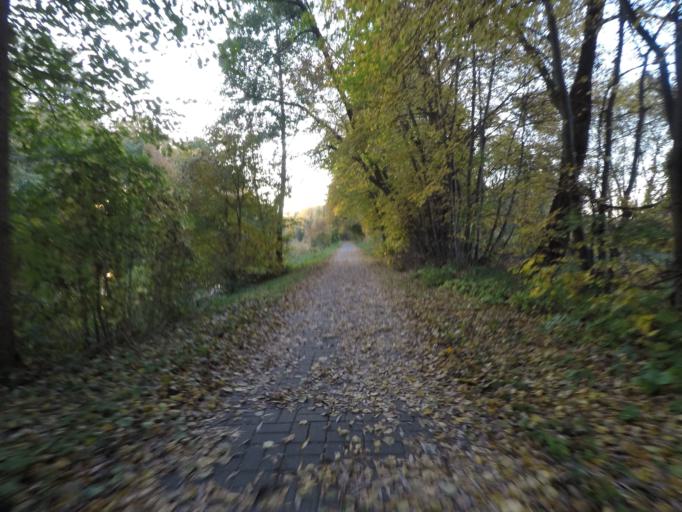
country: DE
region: Brandenburg
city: Melchow
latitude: 52.8459
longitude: 13.6938
